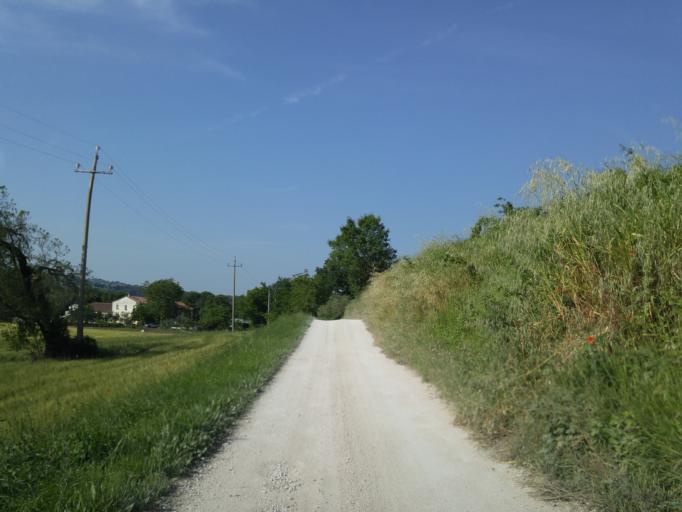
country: IT
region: The Marches
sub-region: Provincia di Pesaro e Urbino
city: Tavernelle
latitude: 43.7237
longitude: 12.8998
